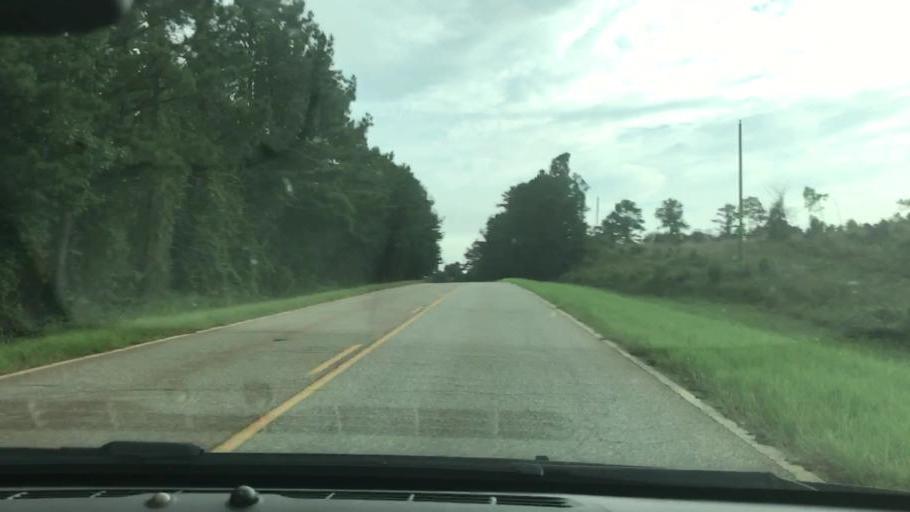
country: US
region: Georgia
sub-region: Quitman County
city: Georgetown
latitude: 31.9234
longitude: -85.0201
